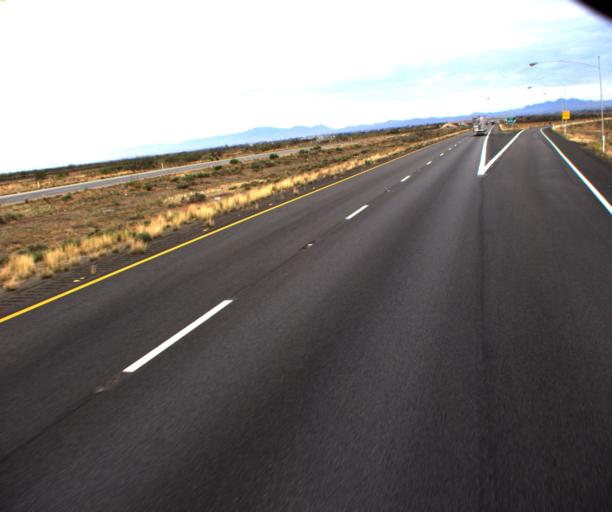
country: US
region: Arizona
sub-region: Cochise County
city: Willcox
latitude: 32.3129
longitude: -109.7905
